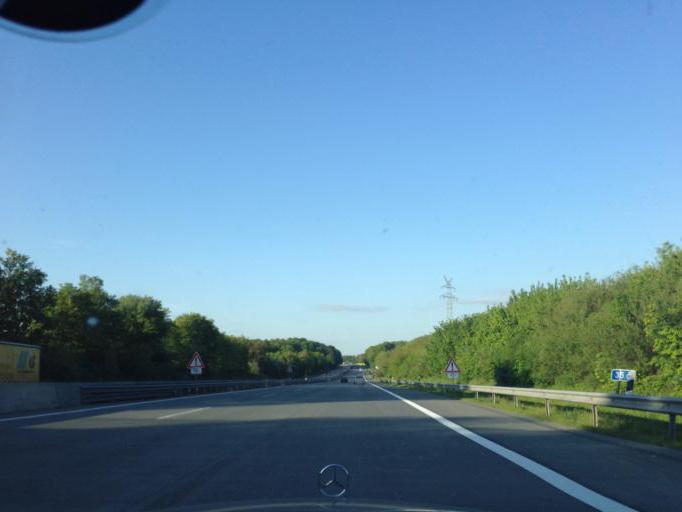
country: DE
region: Schleswig-Holstein
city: Politz
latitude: 53.7689
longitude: 10.3936
